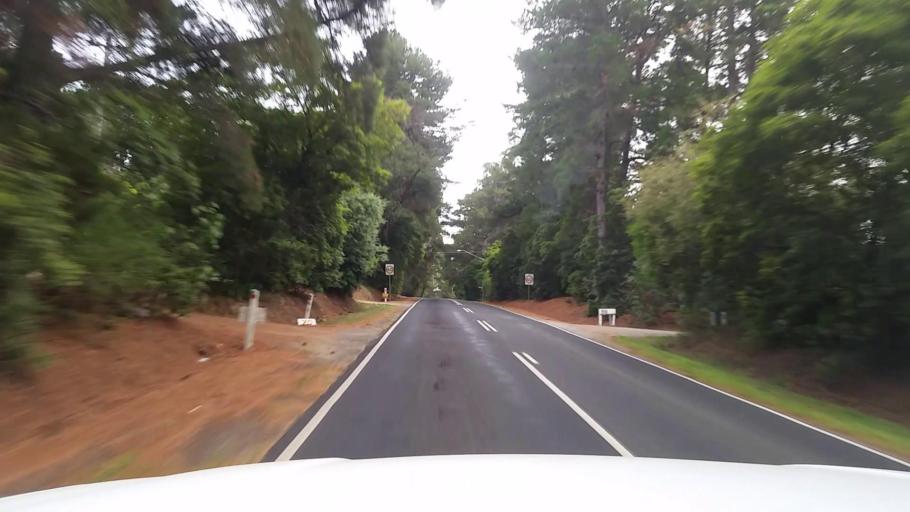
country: AU
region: Victoria
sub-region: Mornington Peninsula
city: Balnarring
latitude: -38.3679
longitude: 145.1211
